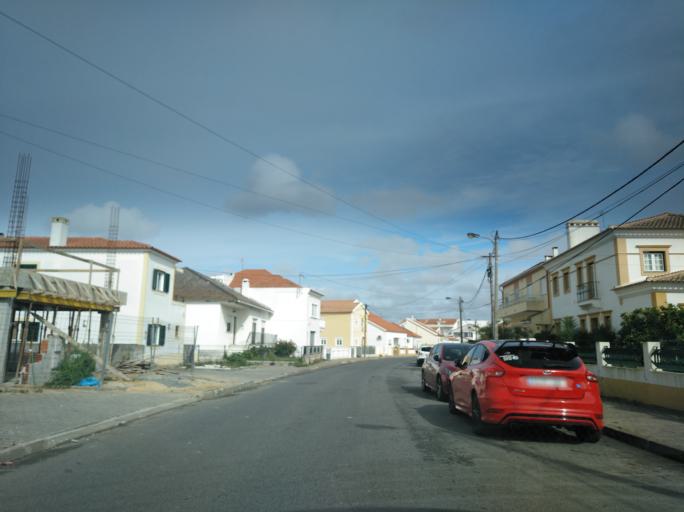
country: PT
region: Setubal
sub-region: Grandola
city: Grandola
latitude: 38.1801
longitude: -8.5694
